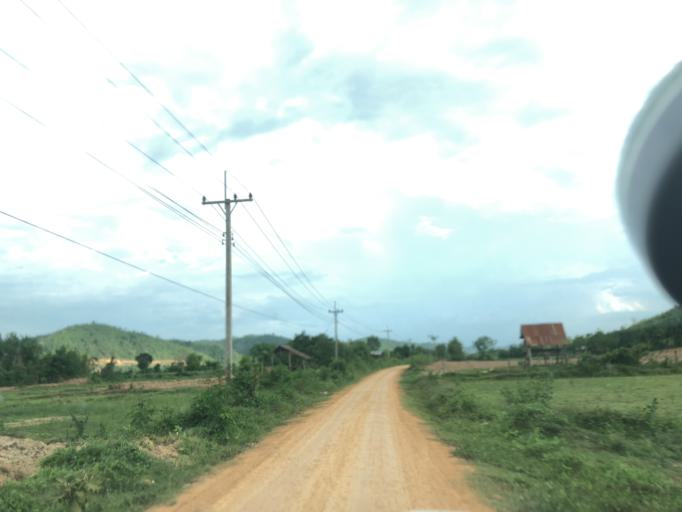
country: TH
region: Loei
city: Chiang Khan
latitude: 17.9951
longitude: 101.4191
